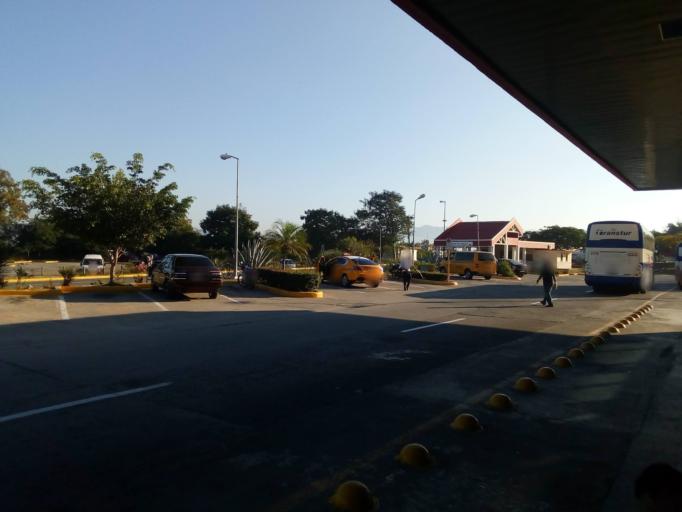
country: CU
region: Santiago de Cuba
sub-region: Municipio de Santiago de Cuba
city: Santiago de Cuba
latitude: 19.9725
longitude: -75.8399
